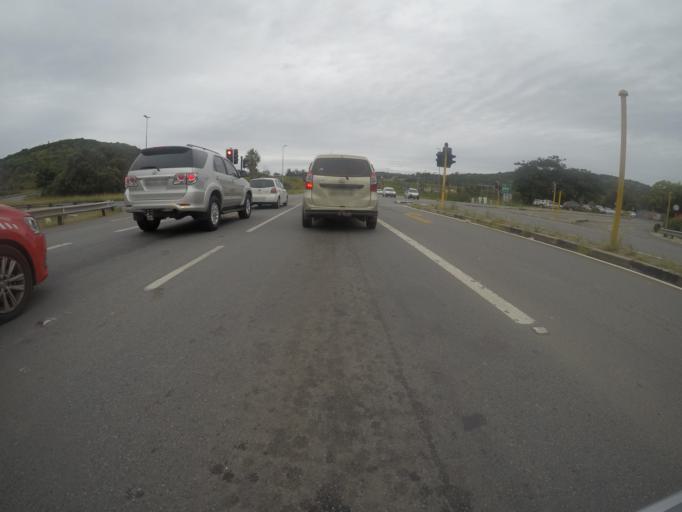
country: ZA
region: Eastern Cape
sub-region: Buffalo City Metropolitan Municipality
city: East London
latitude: -32.9620
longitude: 27.9192
